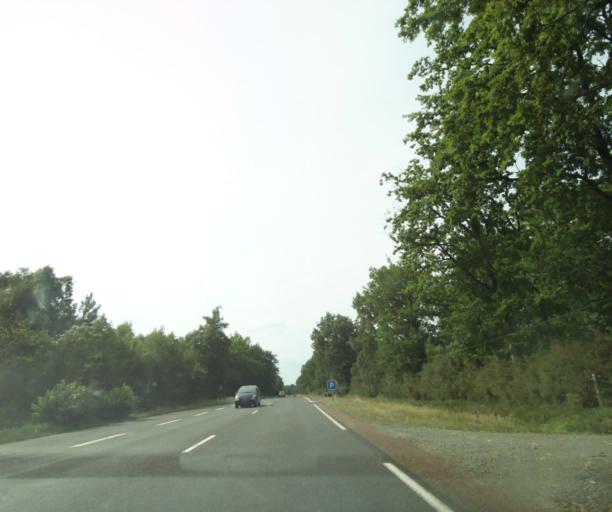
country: FR
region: Pays de la Loire
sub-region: Departement de la Sarthe
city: Marigne-Laille
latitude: 47.7988
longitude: 0.3294
